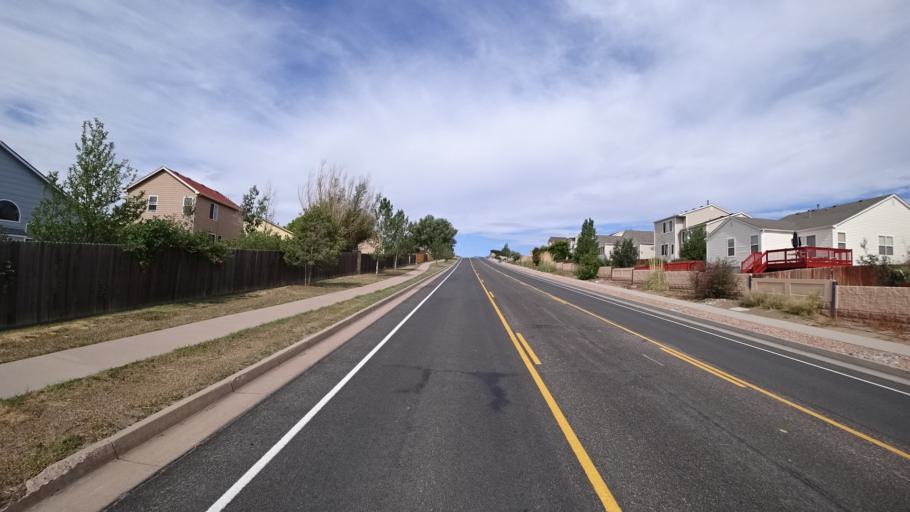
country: US
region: Colorado
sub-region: El Paso County
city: Fountain
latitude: 38.7084
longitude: -104.6884
